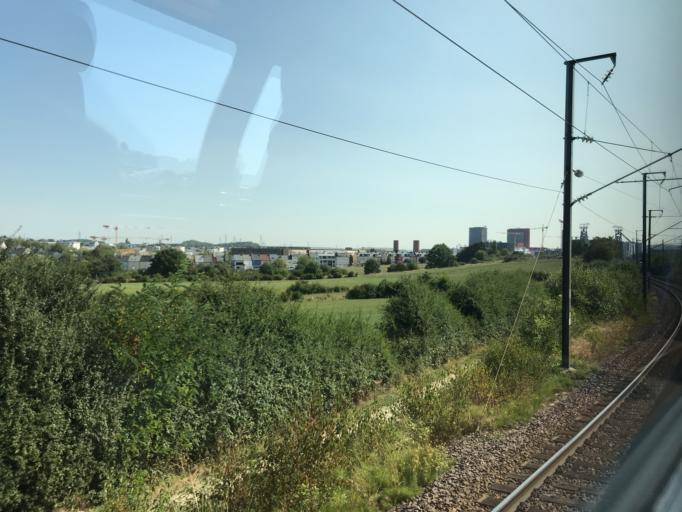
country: LU
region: Luxembourg
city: Belvaux
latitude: 49.5018
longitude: 5.9264
